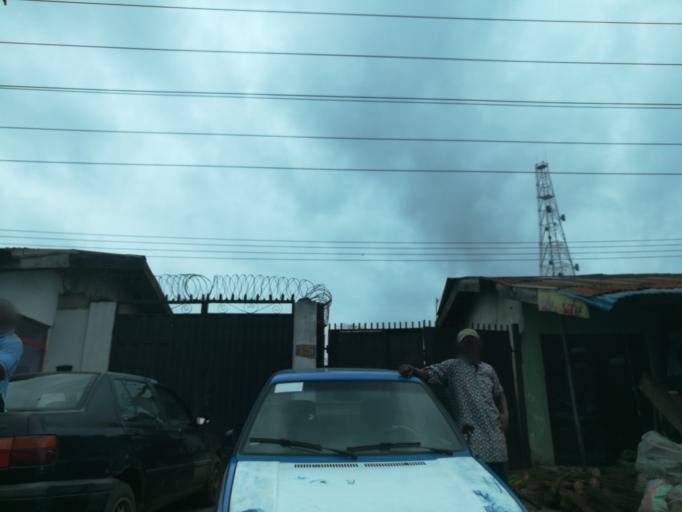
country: NG
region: Rivers
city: Port Harcourt
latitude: 4.8269
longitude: 7.0261
